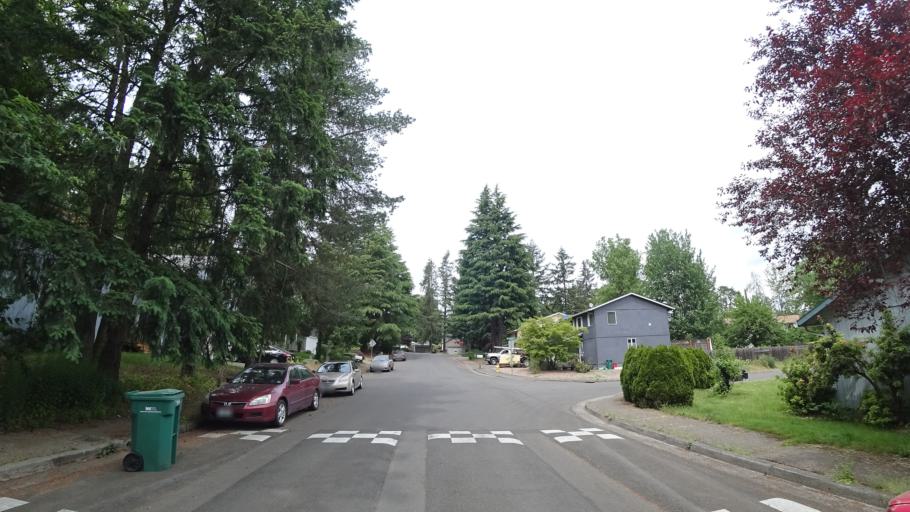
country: US
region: Oregon
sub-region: Washington County
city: Garden Home-Whitford
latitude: 45.4596
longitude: -122.7638
